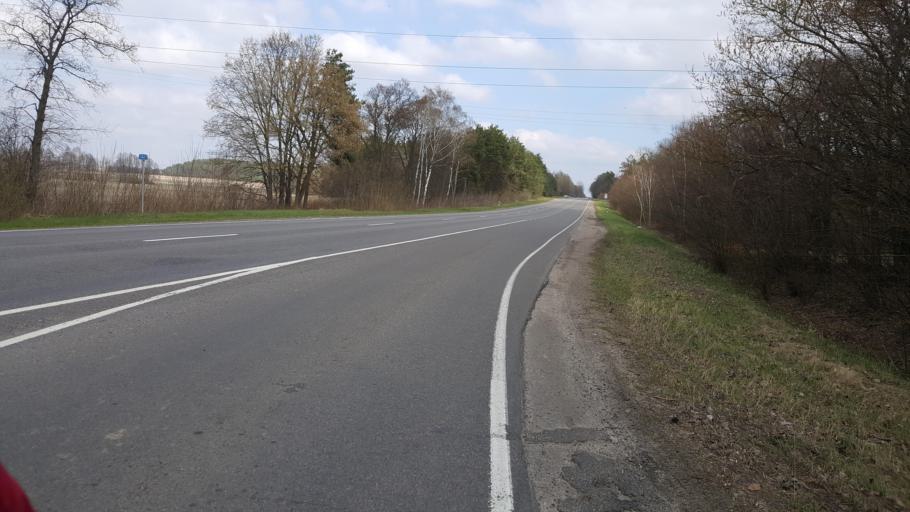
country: BY
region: Brest
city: Kamyanyets
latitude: 52.3410
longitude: 23.9009
